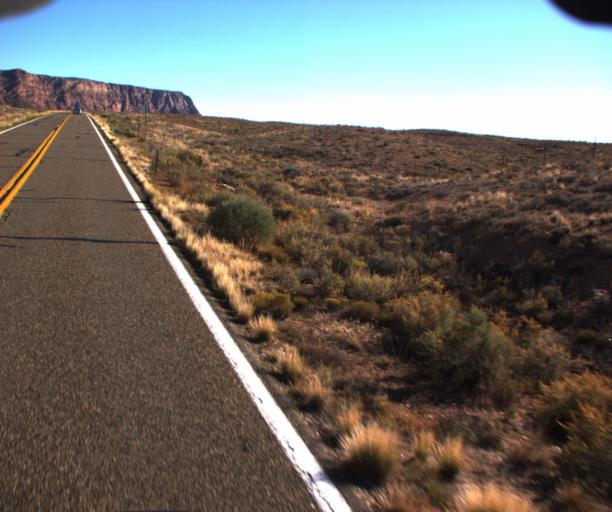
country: US
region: Arizona
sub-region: Coconino County
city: LeChee
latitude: 36.6695
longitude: -111.6530
